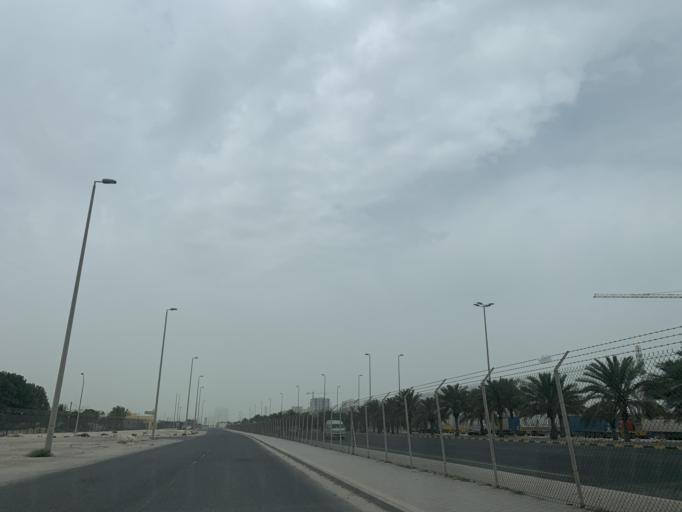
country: BH
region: Muharraq
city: Al Hadd
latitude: 26.2250
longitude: 50.6644
